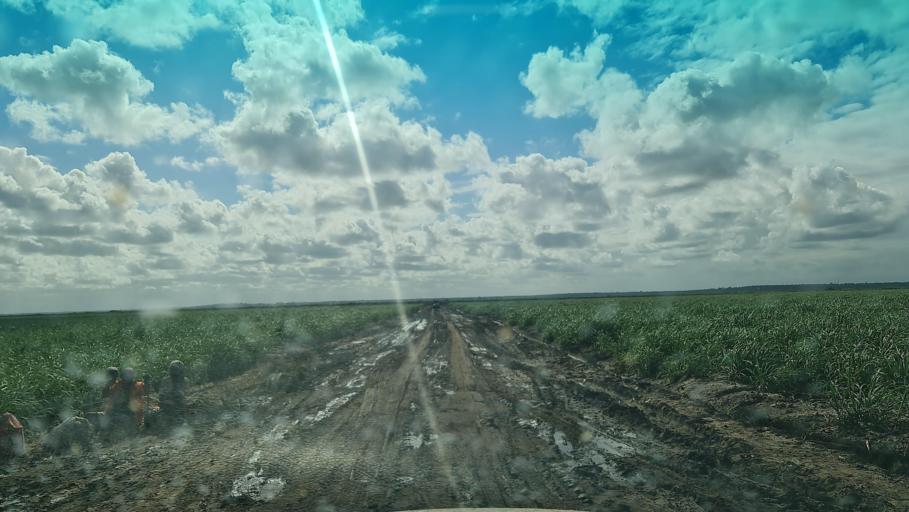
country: MZ
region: Maputo
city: Manhica
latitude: -25.4393
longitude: 32.8600
